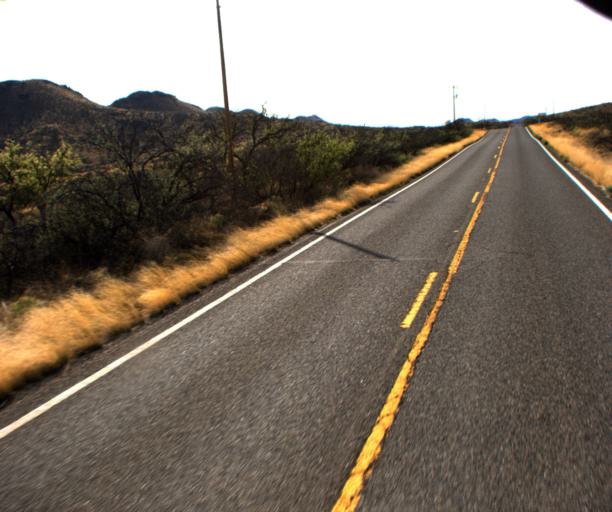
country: US
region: Arizona
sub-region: Cochise County
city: Willcox
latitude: 32.1695
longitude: -109.5936
